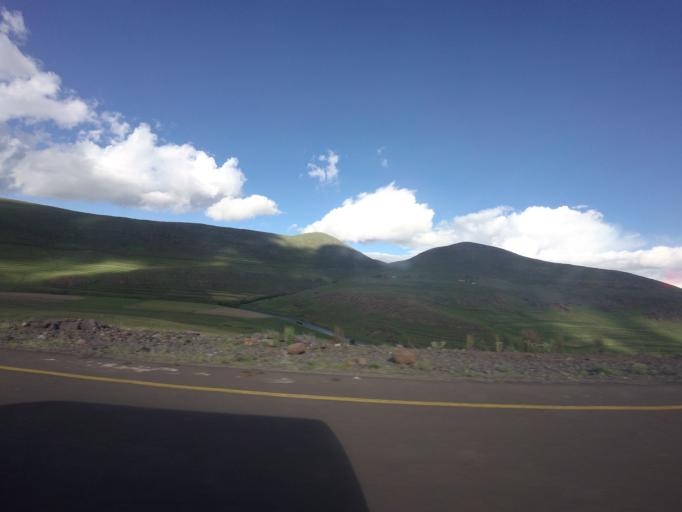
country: LS
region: Maseru
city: Nako
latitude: -29.8001
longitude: 28.0328
